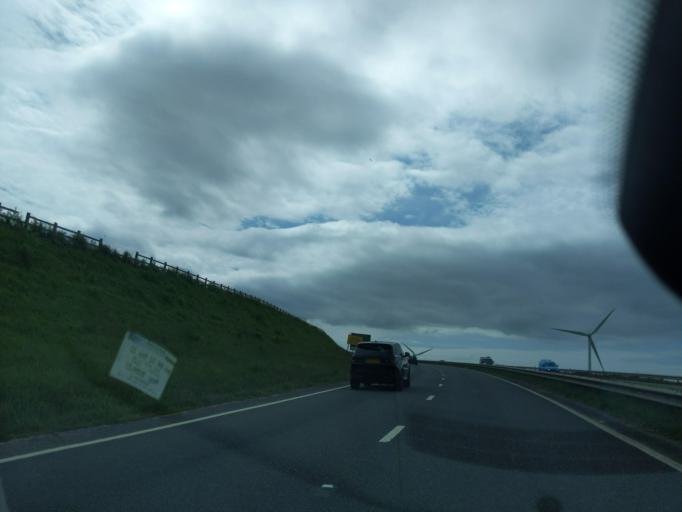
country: GB
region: England
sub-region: Cornwall
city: Newquay
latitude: 50.3494
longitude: -5.0195
